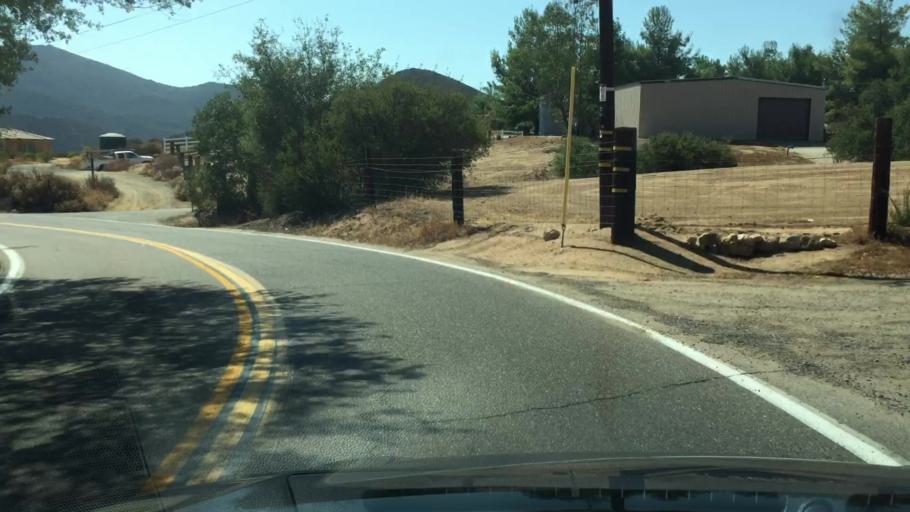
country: US
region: California
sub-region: San Diego County
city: Alpine
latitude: 32.7555
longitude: -116.7700
